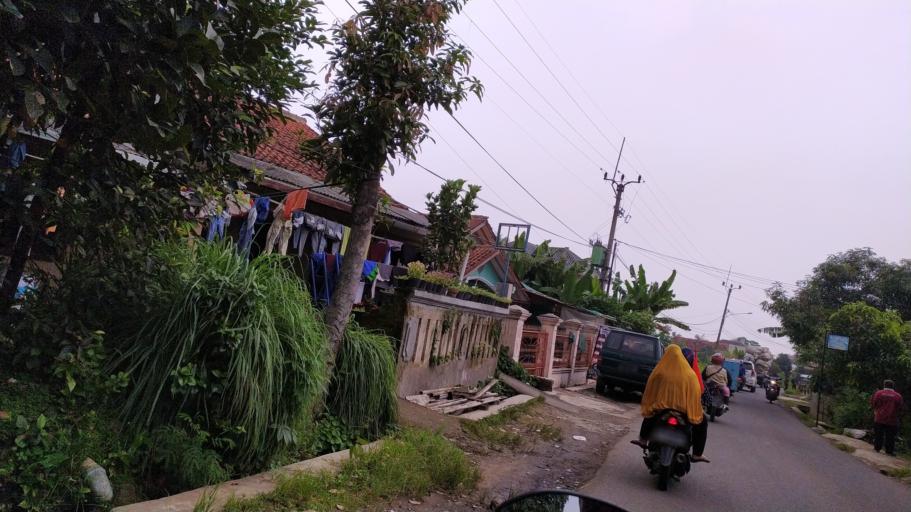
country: ID
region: West Java
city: Ciampea
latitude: -6.6029
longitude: 106.7025
